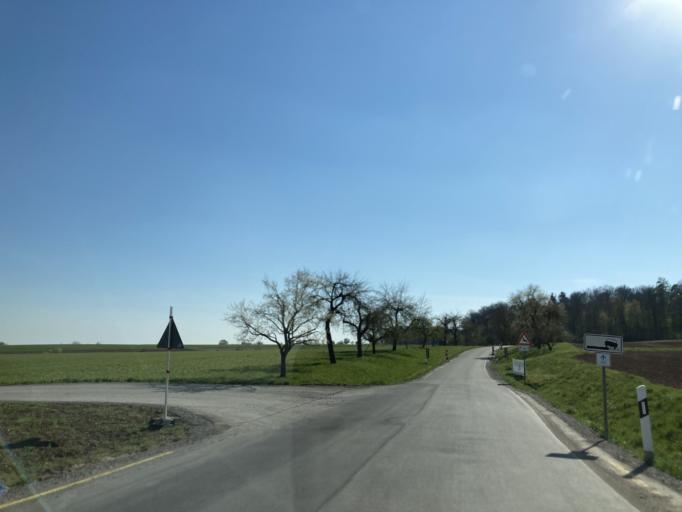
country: DE
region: Baden-Wuerttemberg
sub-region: Regierungsbezirk Stuttgart
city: Hildrizhausen
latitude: 48.5601
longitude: 8.9507
